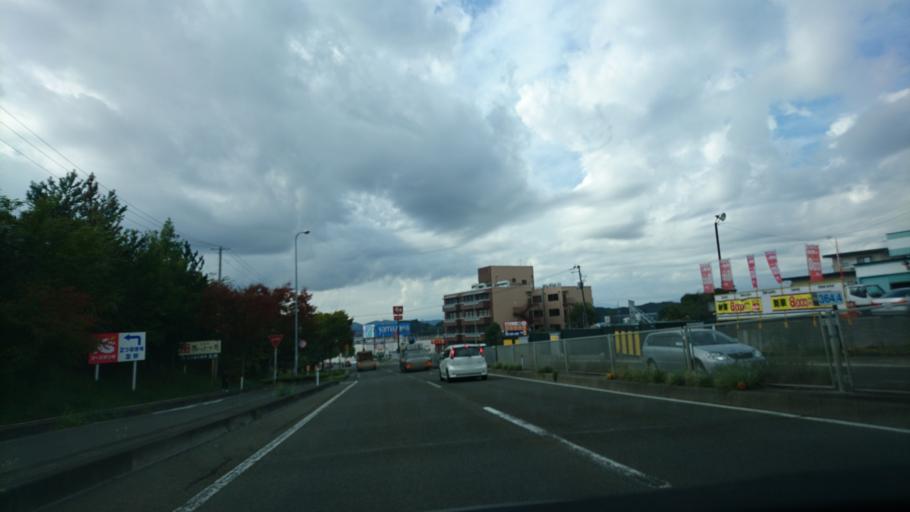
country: JP
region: Miyagi
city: Tomiya
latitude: 38.3579
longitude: 140.8723
